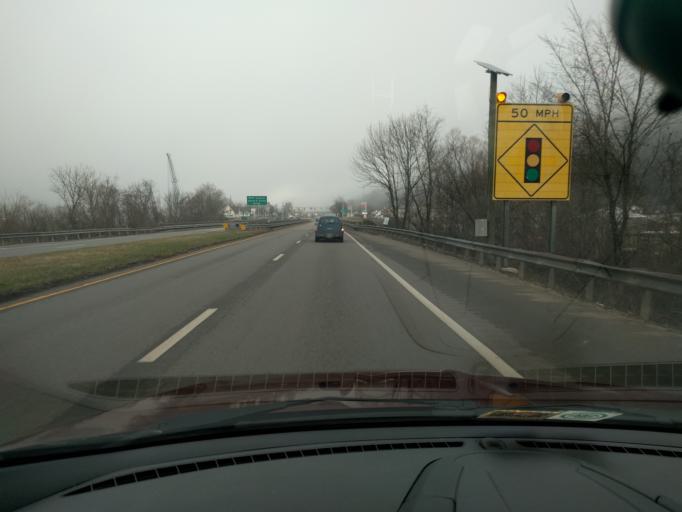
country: US
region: West Virginia
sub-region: Kanawha County
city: Chesapeake
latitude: 38.2190
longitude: -81.5219
